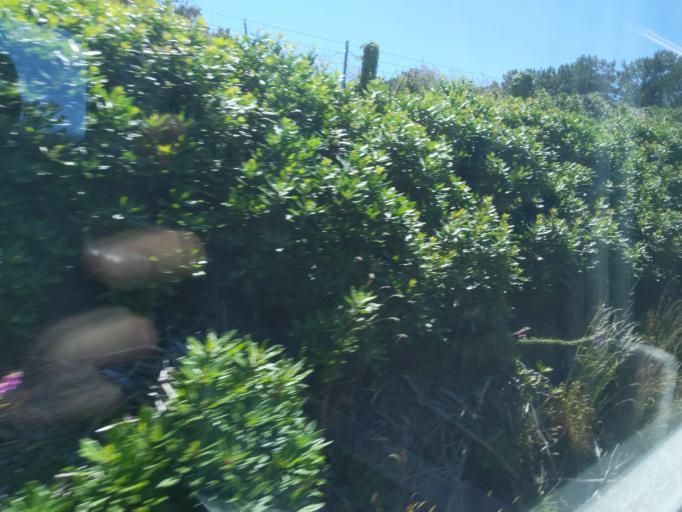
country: GB
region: England
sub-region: Cornwall
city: Chacewater
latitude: 50.2660
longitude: -5.1787
